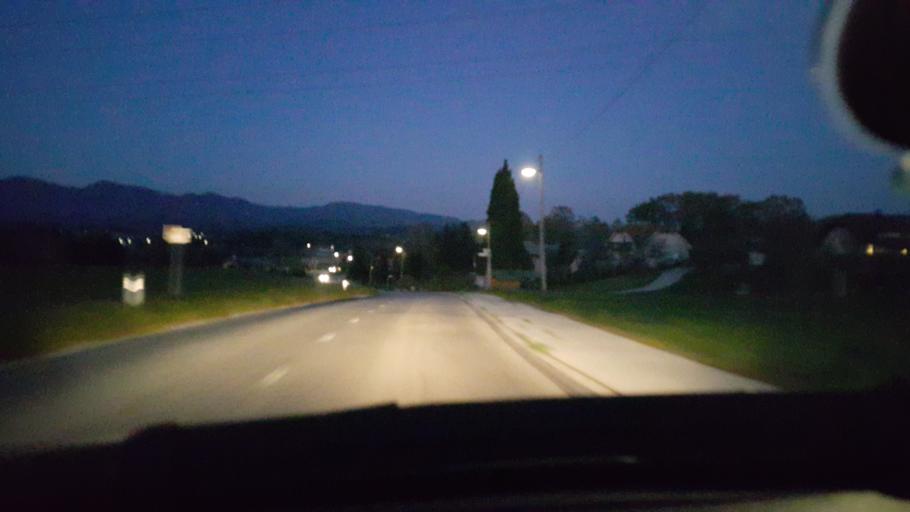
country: SI
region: Store
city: Store
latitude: 46.2380
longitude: 15.3116
